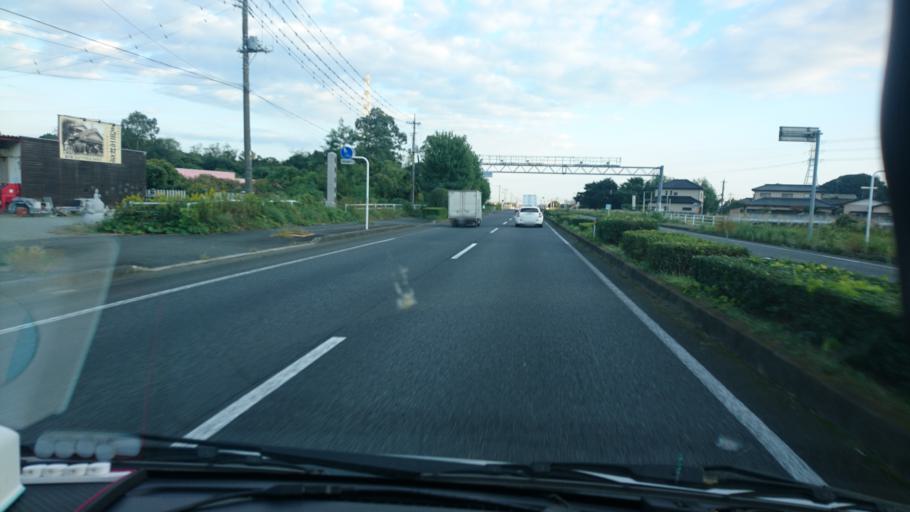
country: JP
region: Gunma
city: Kiryu
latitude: 36.3633
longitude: 139.3672
